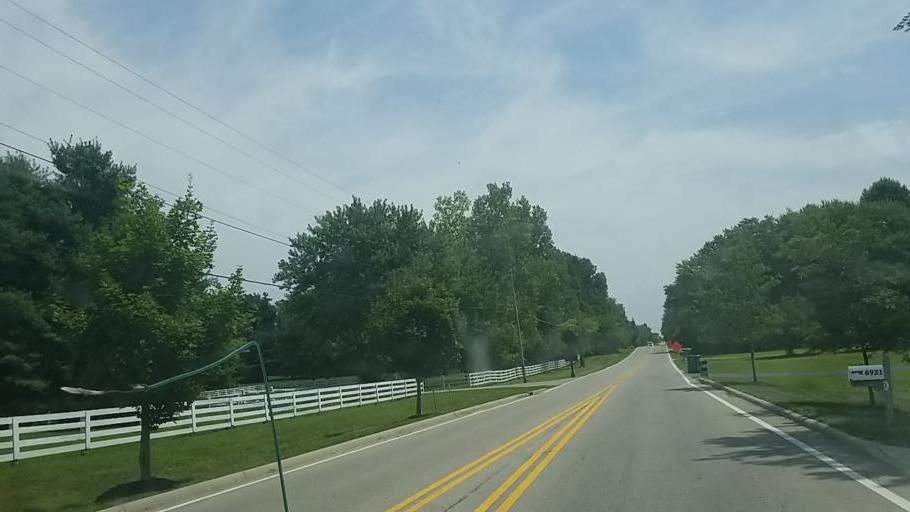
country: US
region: Ohio
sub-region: Franklin County
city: New Albany
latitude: 40.0529
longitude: -82.8083
